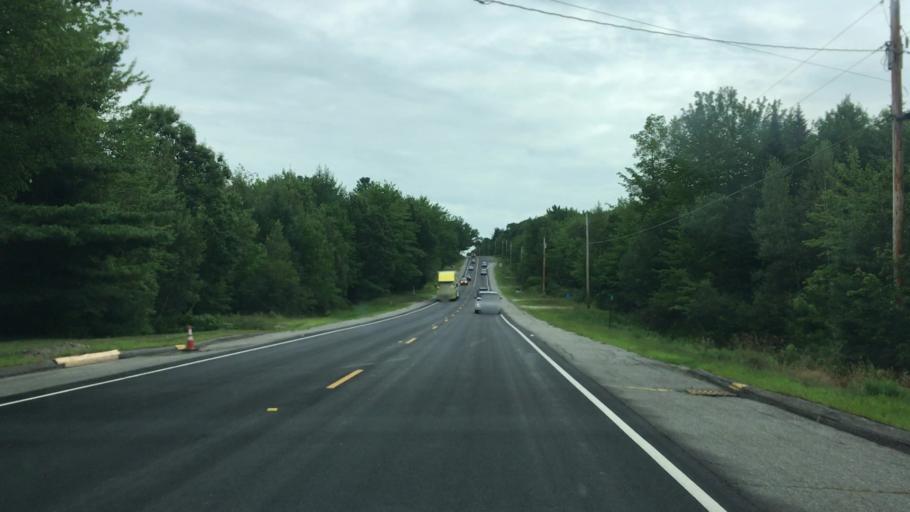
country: US
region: Maine
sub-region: Washington County
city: Addison
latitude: 44.9439
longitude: -67.7082
